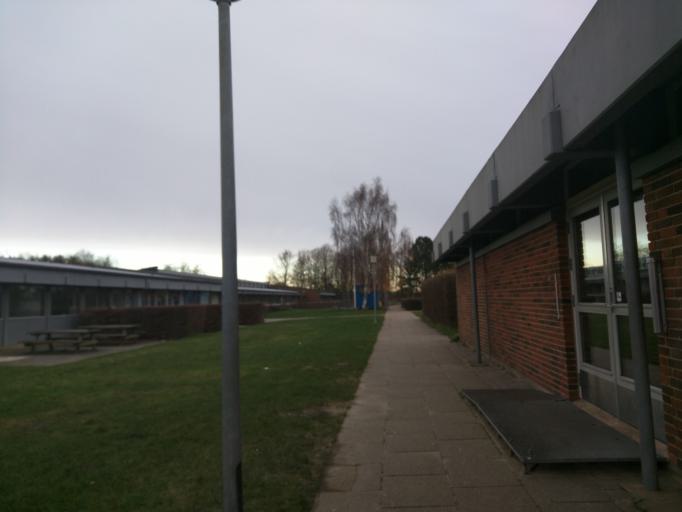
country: DK
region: Central Jutland
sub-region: Viborg Kommune
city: Viborg
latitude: 56.4419
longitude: 9.3796
